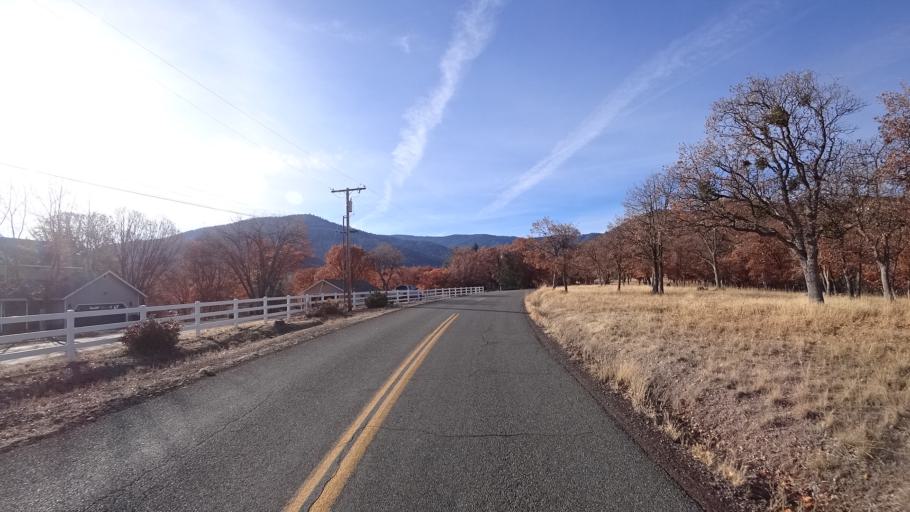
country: US
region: California
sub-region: Siskiyou County
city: Yreka
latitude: 41.6644
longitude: -122.6210
